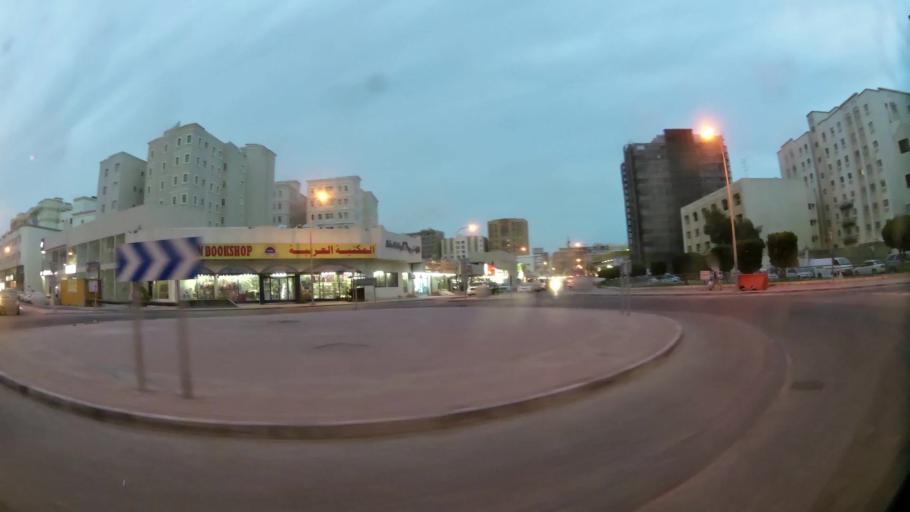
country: QA
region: Baladiyat ad Dawhah
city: Doha
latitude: 25.2722
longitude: 51.5238
